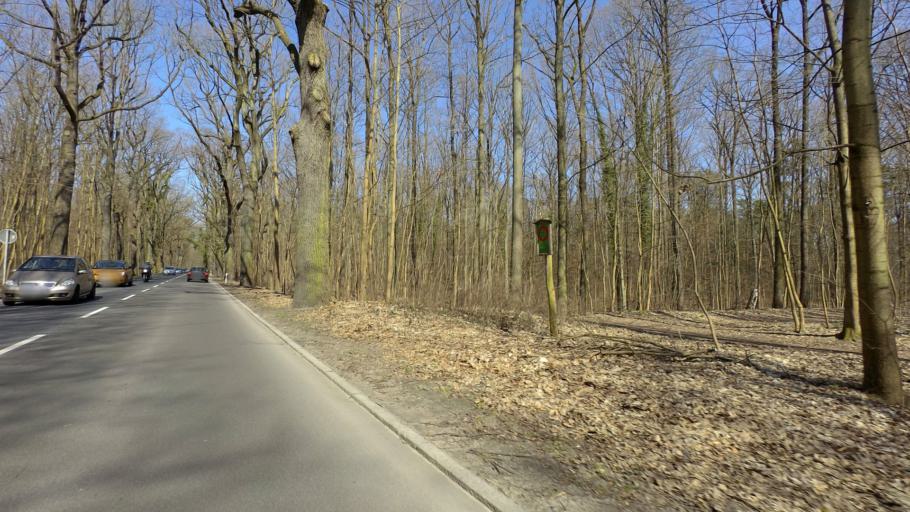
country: DE
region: Berlin
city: Frohnau
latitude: 52.6456
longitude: 13.2991
